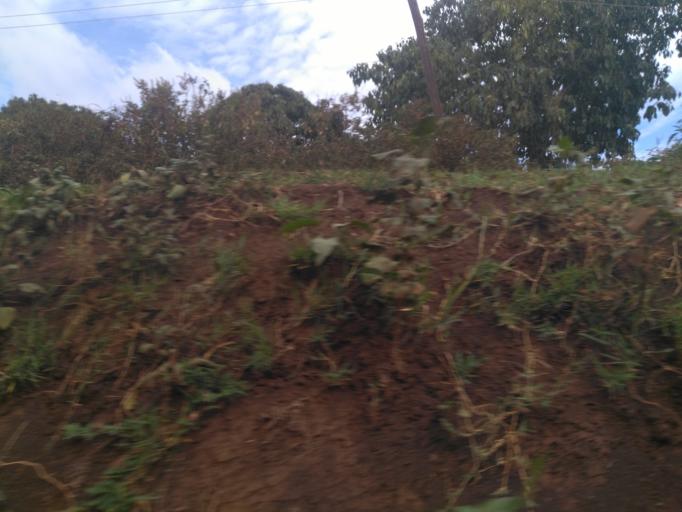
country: UG
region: Central Region
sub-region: Buikwe District
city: Njeru
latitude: 0.4129
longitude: 33.1823
